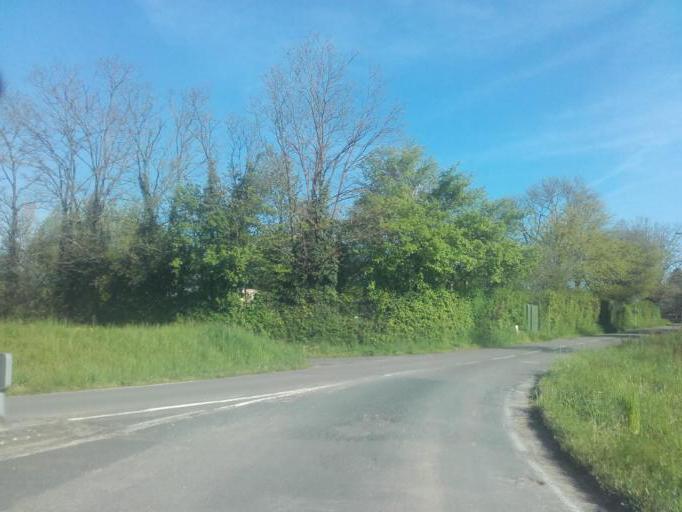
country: FR
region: Bourgogne
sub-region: Departement de Saone-et-Loire
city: Charnay-les-Macon
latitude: 46.2907
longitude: 4.7842
